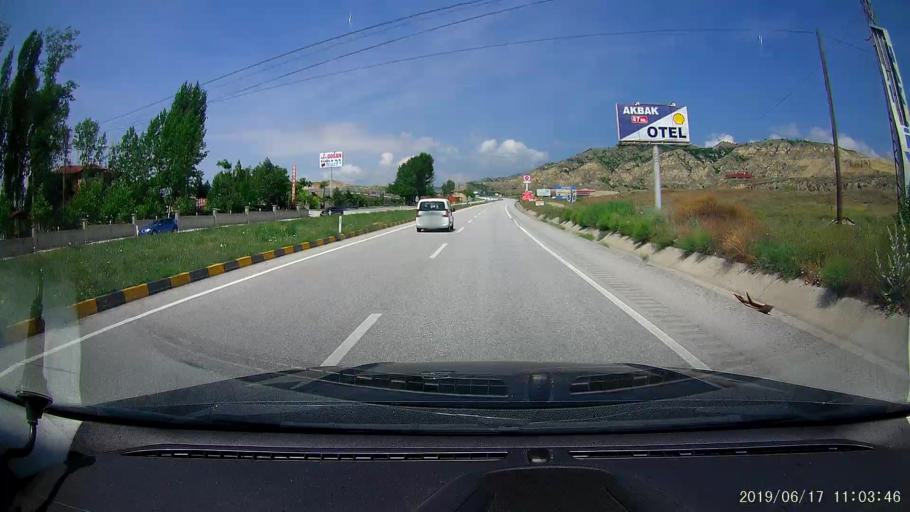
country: TR
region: Kastamonu
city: Tosya
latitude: 41.0192
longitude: 34.1097
